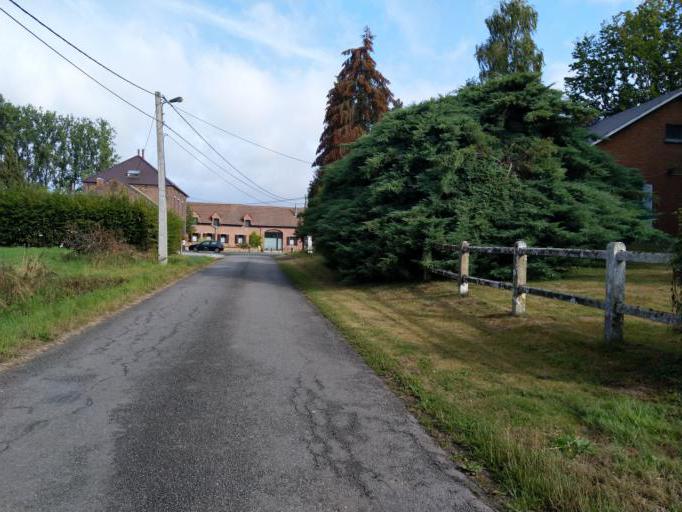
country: BE
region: Wallonia
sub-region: Province du Hainaut
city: Jurbise
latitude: 50.5342
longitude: 3.8833
